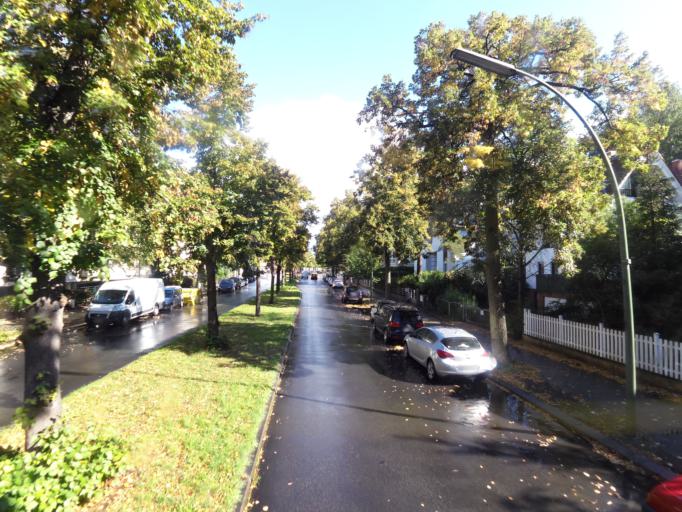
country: DE
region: Berlin
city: Schmargendorf
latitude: 52.4756
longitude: 13.2884
